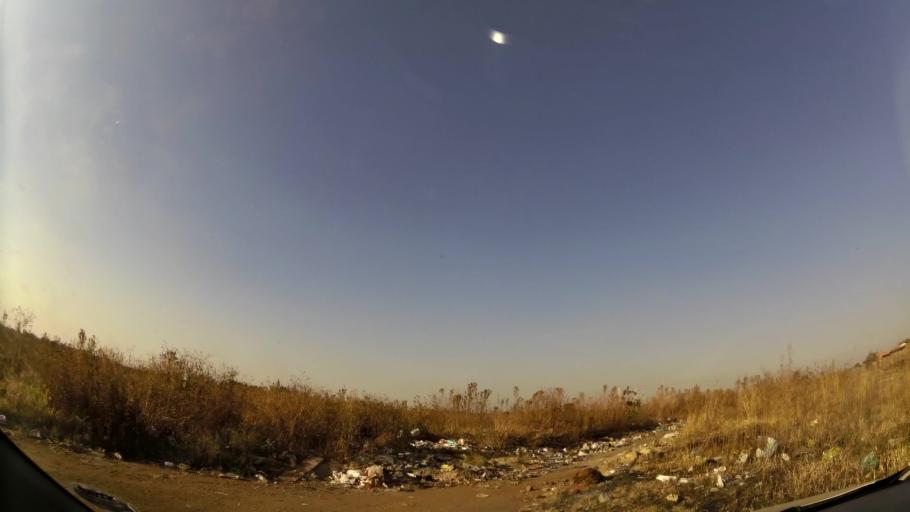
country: ZA
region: Gauteng
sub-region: West Rand District Municipality
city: Randfontein
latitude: -26.1968
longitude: 27.7017
